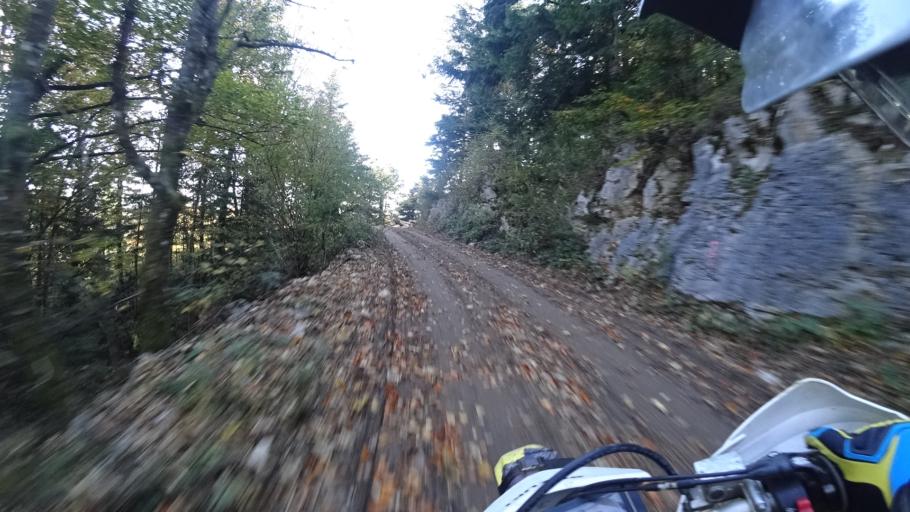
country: HR
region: Karlovacka
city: Plaski
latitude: 45.0250
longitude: 15.3900
